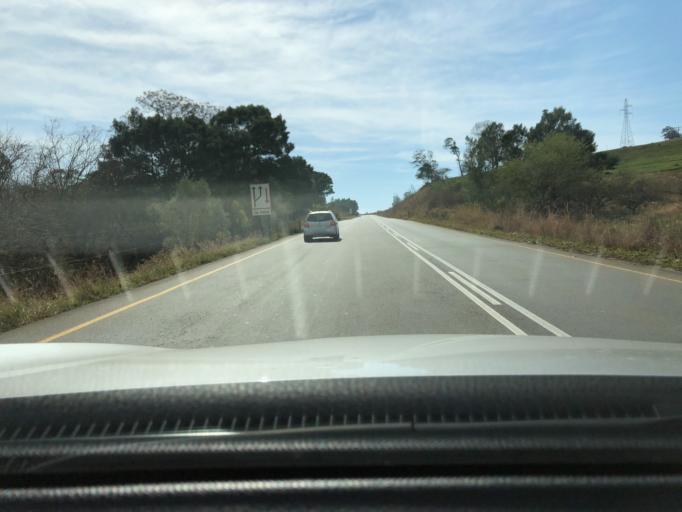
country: ZA
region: KwaZulu-Natal
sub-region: Sisonke District Municipality
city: Ixopo
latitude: -30.0728
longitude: 30.1640
